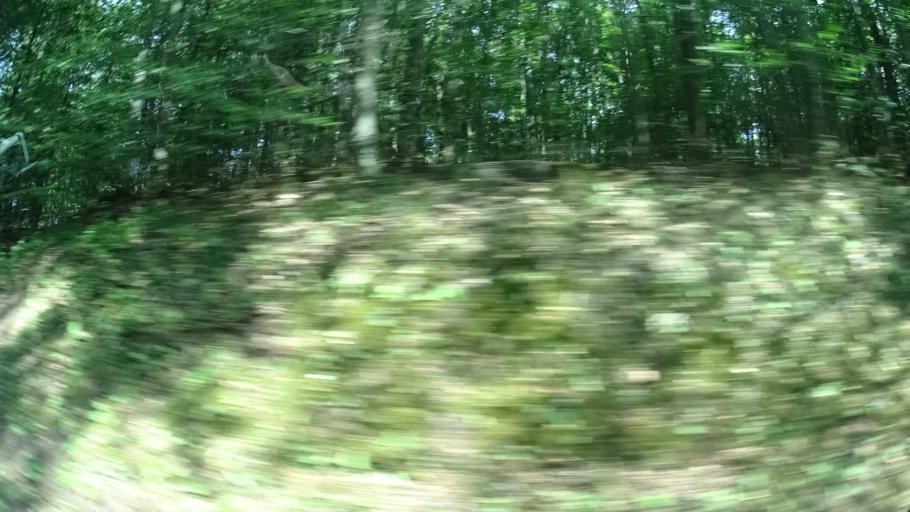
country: DE
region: Hesse
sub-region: Regierungsbezirk Giessen
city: Lauterbach
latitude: 50.5864
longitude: 9.4238
